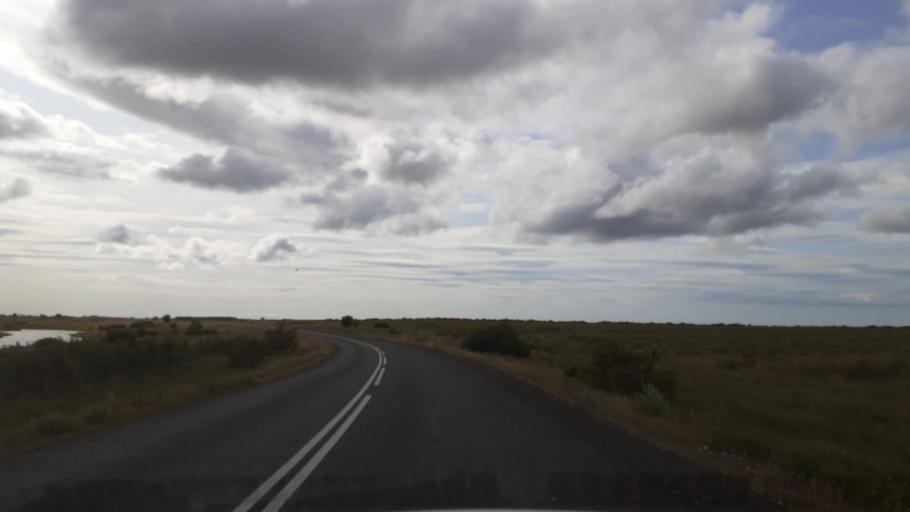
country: IS
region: South
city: Vestmannaeyjar
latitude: 63.8270
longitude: -20.4274
